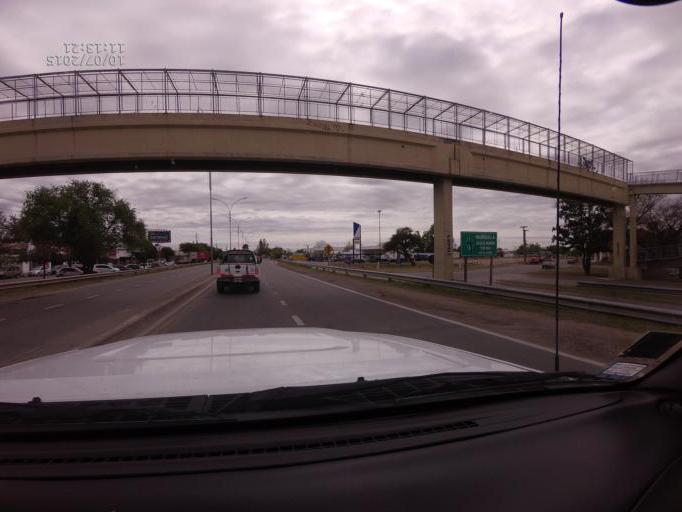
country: AR
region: Cordoba
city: Jesus Maria
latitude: -30.9788
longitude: -64.0855
